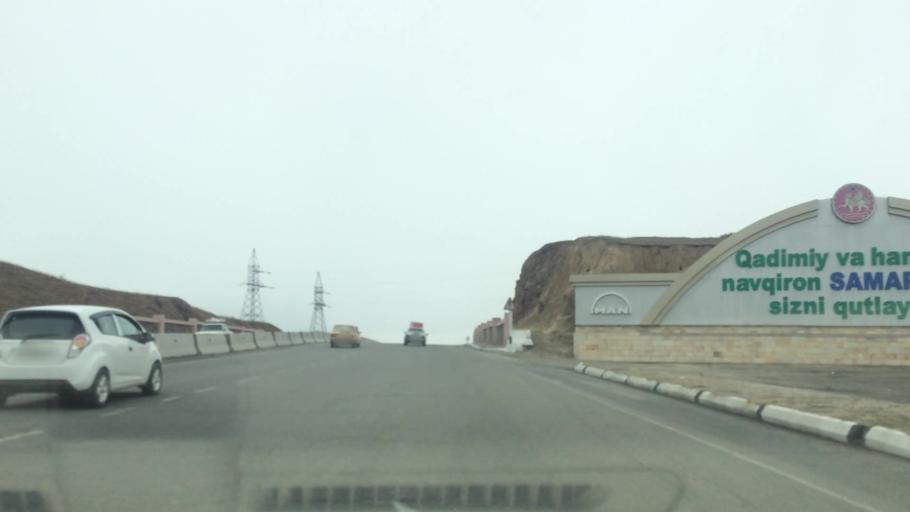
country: UZ
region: Samarqand
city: Jomboy
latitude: 39.6871
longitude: 67.0521
